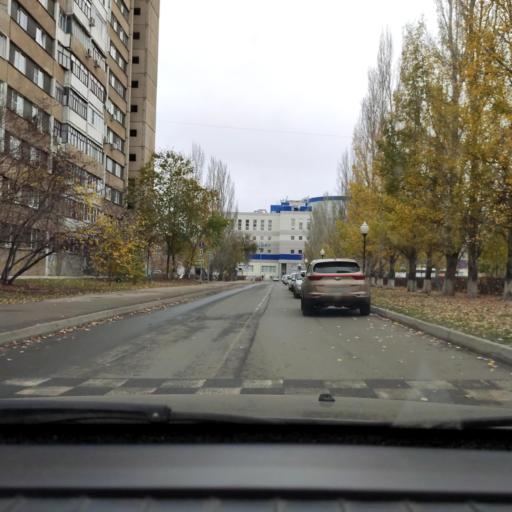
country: RU
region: Samara
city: Tol'yatti
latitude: 53.5318
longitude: 49.3189
